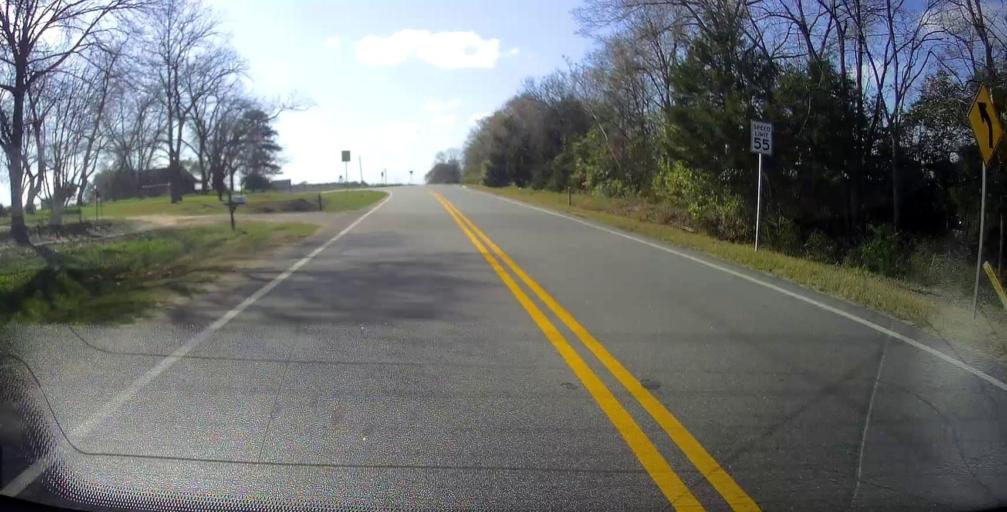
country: US
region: Georgia
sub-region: Dodge County
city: Eastman
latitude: 32.1967
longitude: -83.2042
